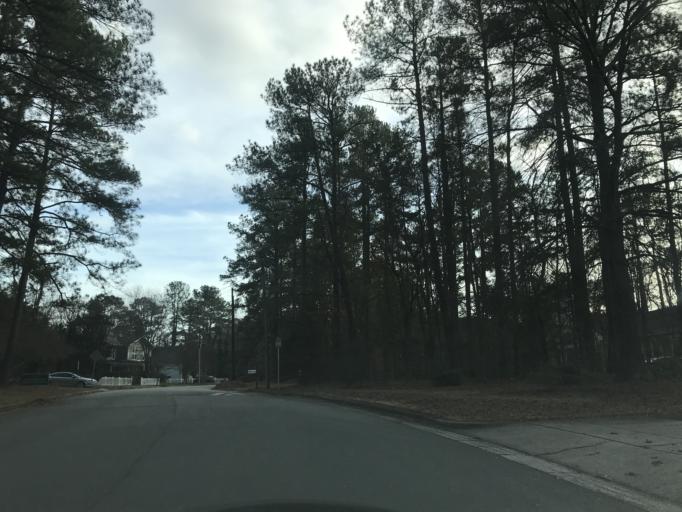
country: US
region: North Carolina
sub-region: Wake County
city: Raleigh
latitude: 35.7962
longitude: -78.6179
